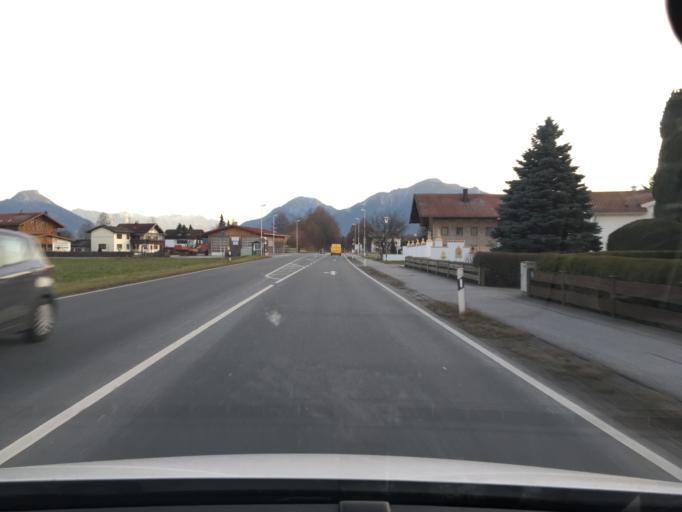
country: DE
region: Bavaria
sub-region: Upper Bavaria
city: Raubling
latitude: 47.7701
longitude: 12.1058
